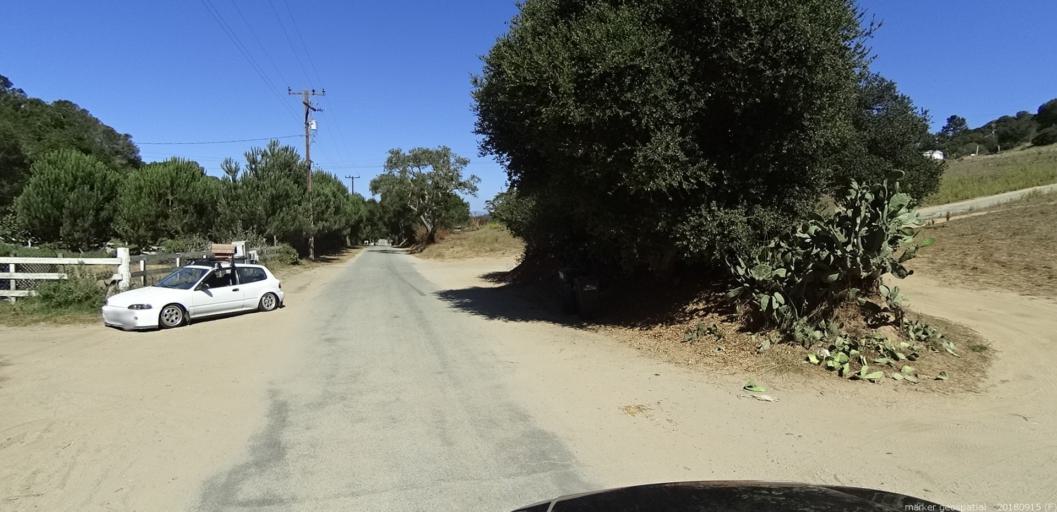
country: US
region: California
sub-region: Monterey County
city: Las Lomas
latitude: 36.8442
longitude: -121.7053
